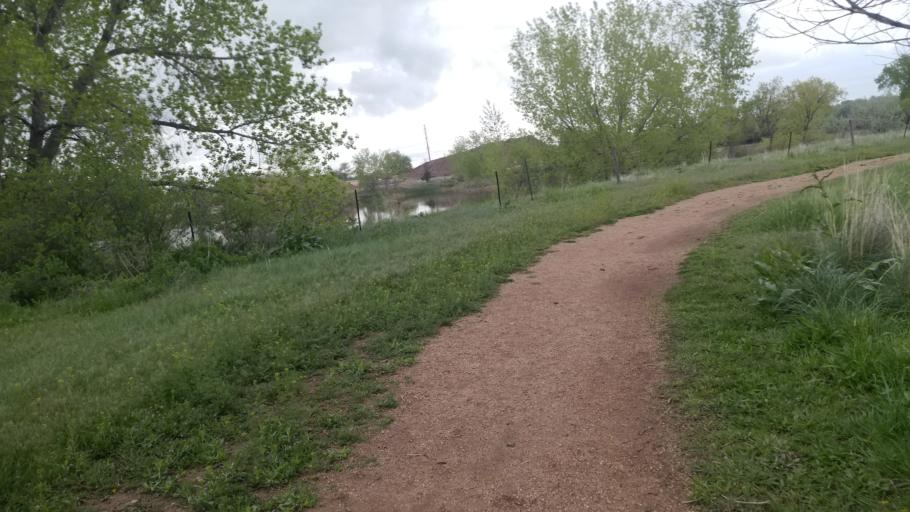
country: US
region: Colorado
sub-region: Boulder County
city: Gunbarrel
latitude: 40.0436
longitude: -105.1880
